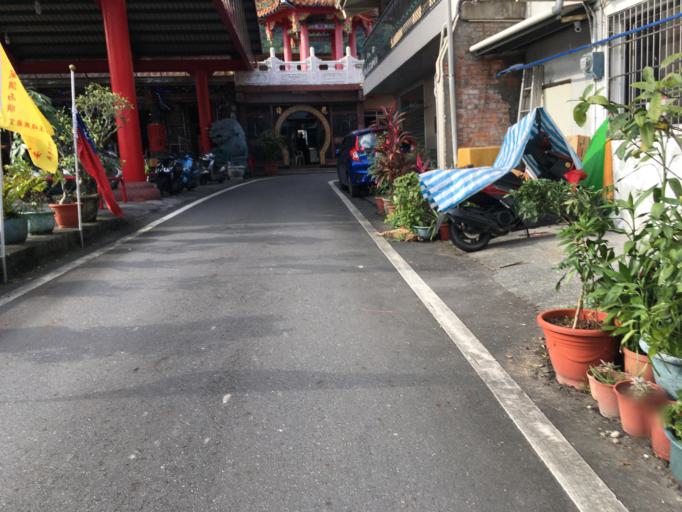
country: TW
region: Taiwan
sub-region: Yilan
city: Yilan
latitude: 24.8374
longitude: 121.7839
